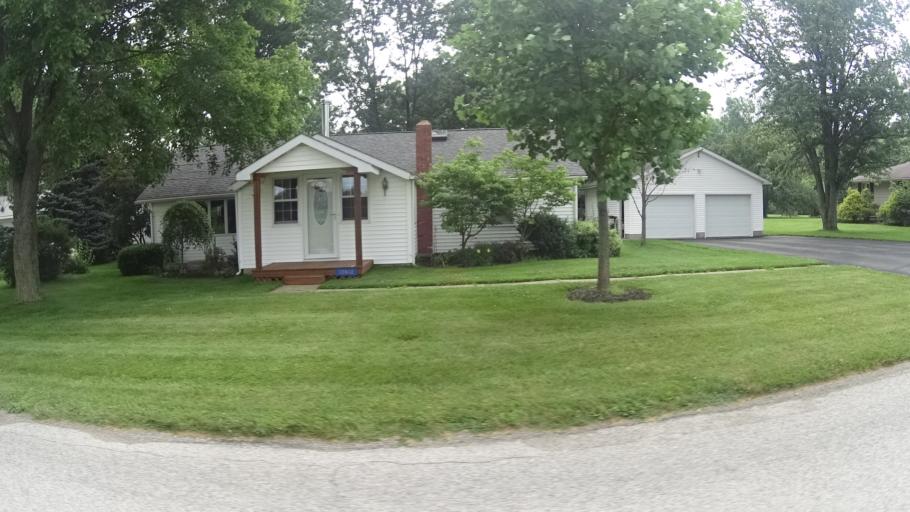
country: US
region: Ohio
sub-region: Huron County
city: Wakeman
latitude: 41.3048
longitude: -82.4812
